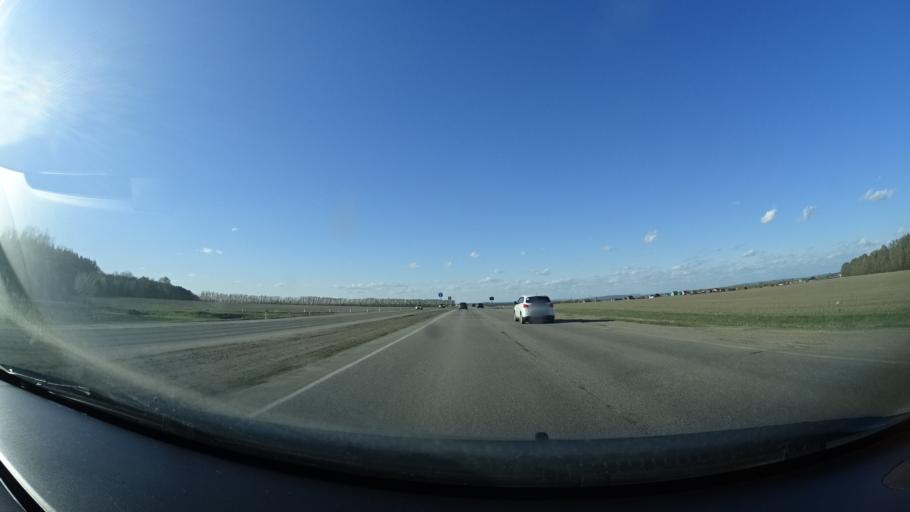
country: RU
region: Bashkortostan
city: Kabakovo
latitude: 54.4625
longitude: 55.9150
